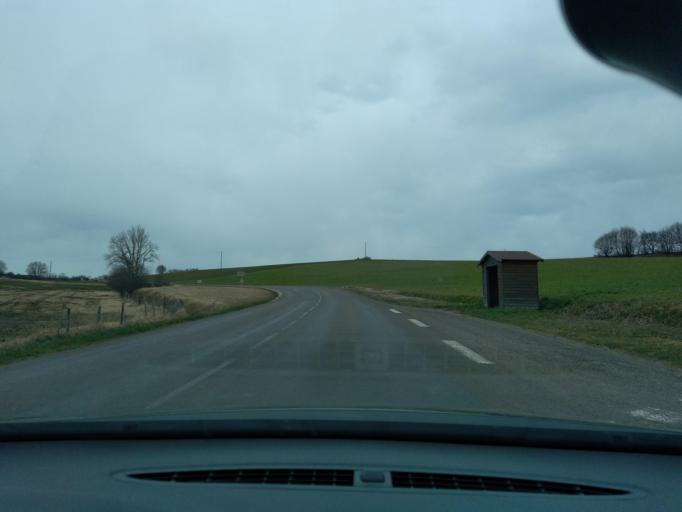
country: FR
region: Franche-Comte
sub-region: Departement du Jura
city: Arinthod
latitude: 46.4406
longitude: 5.5613
